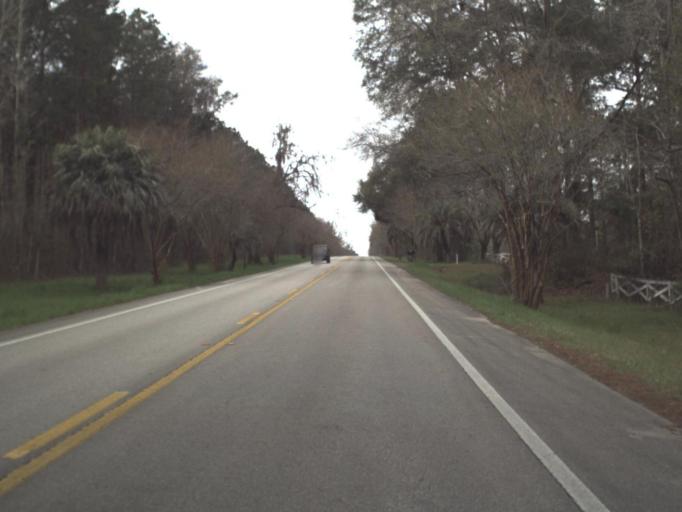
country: US
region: Florida
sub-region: Jefferson County
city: Monticello
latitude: 30.5388
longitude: -83.9229
